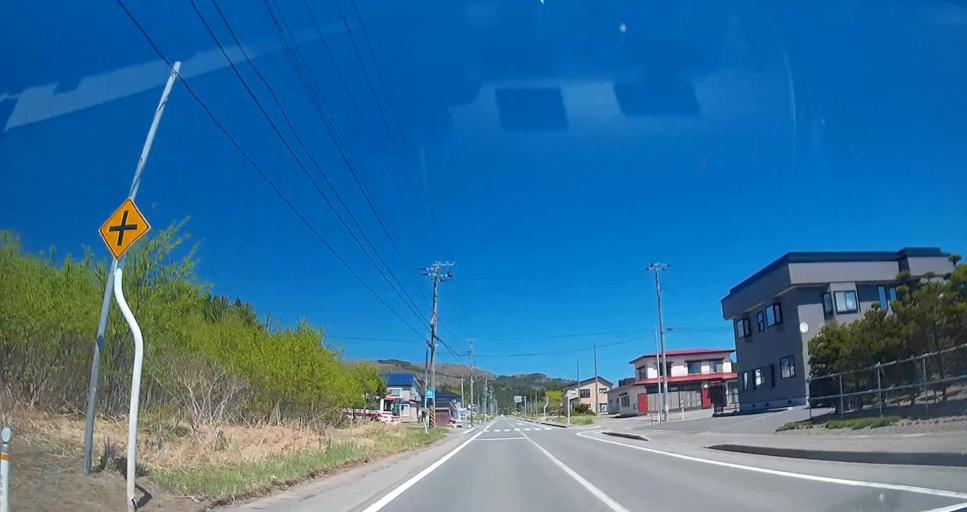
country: JP
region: Aomori
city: Mutsu
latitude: 41.0818
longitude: 141.3858
